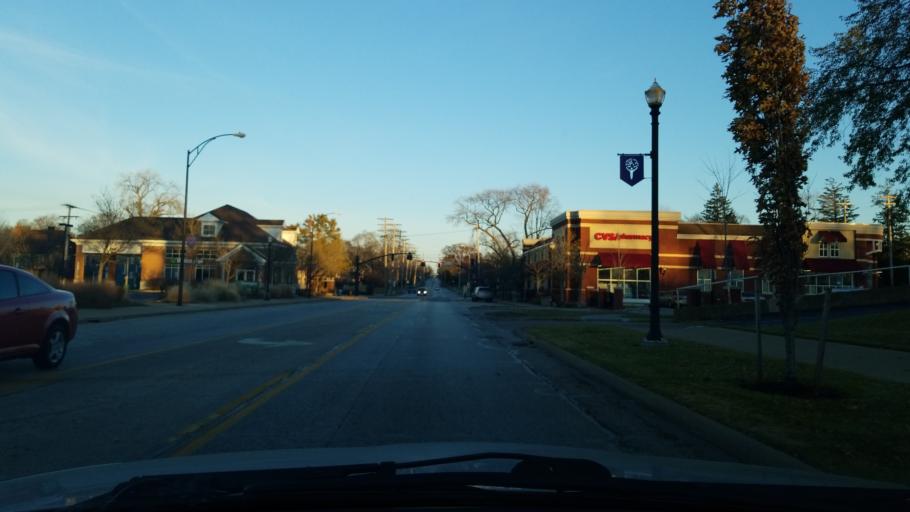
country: US
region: Ohio
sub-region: Cuyahoga County
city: Shaker Heights
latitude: 41.4645
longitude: -81.5604
